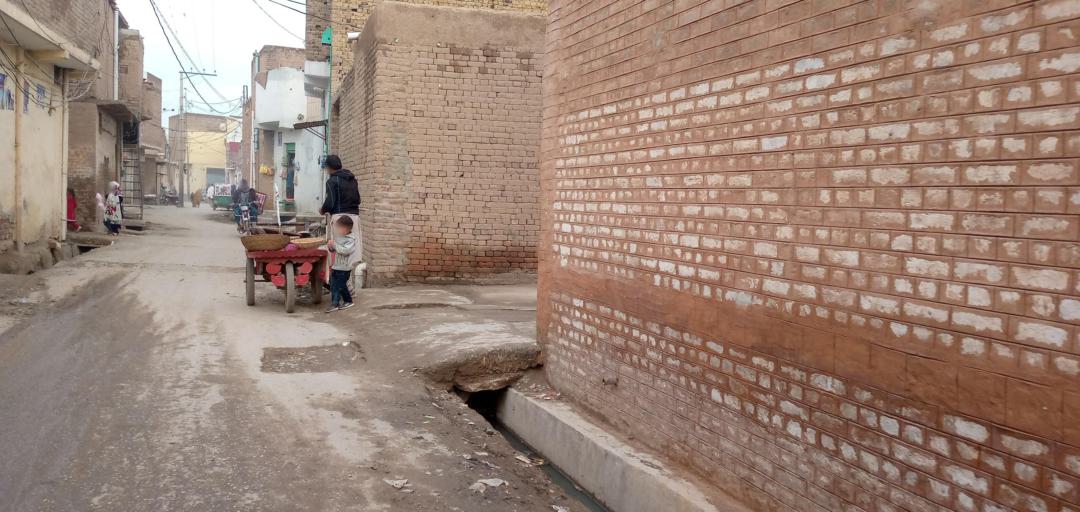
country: PK
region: Khyber Pakhtunkhwa
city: Peshawar
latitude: 34.0142
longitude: 71.5021
